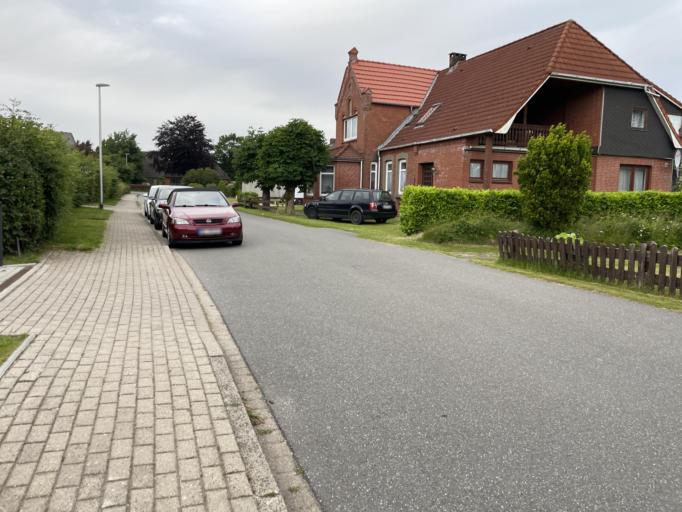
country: DE
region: Schleswig-Holstein
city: Mildstedt
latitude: 54.4607
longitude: 9.0931
